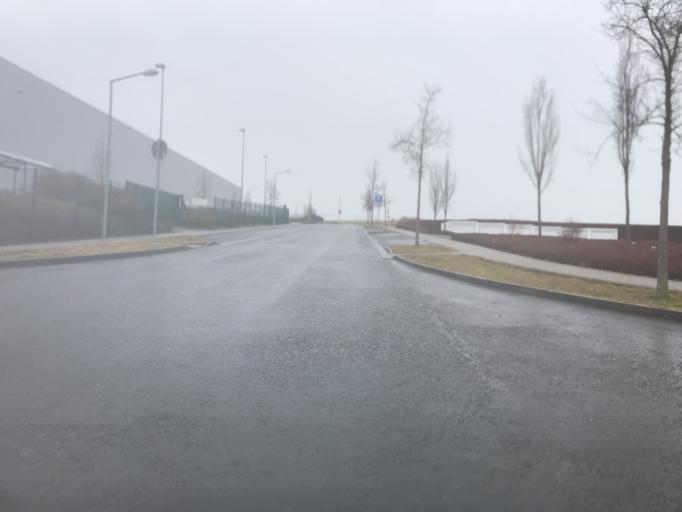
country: DE
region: Rheinland-Pfalz
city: Nieder-Olm
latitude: 49.9109
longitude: 8.1767
